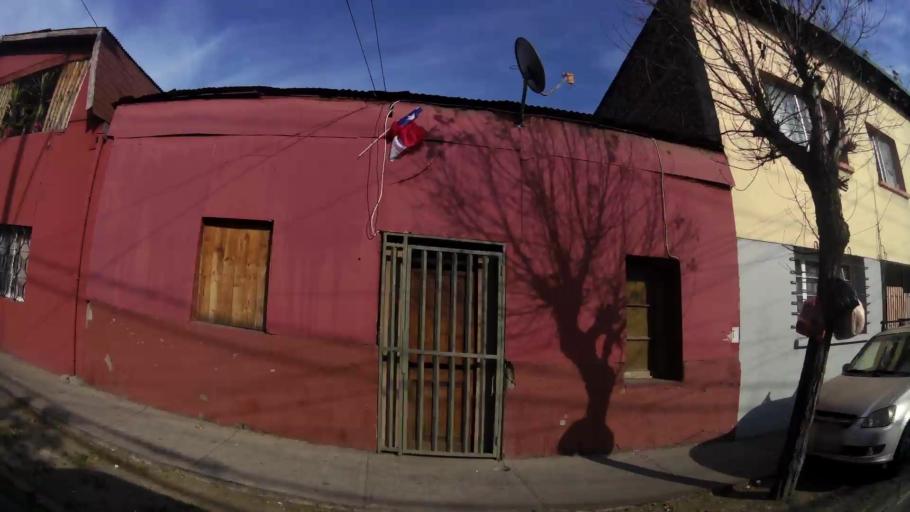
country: CL
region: Santiago Metropolitan
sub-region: Provincia de Santiago
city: Santiago
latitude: -33.5153
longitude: -70.6630
